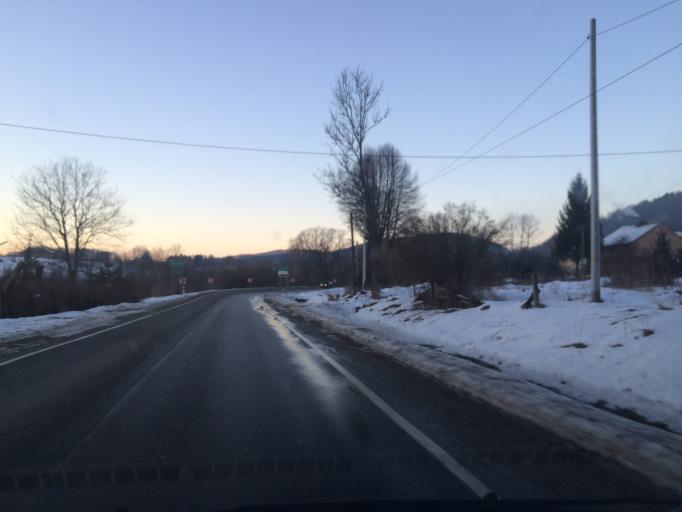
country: PL
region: Subcarpathian Voivodeship
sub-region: Powiat bieszczadzki
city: Czarna
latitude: 49.3788
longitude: 22.6422
